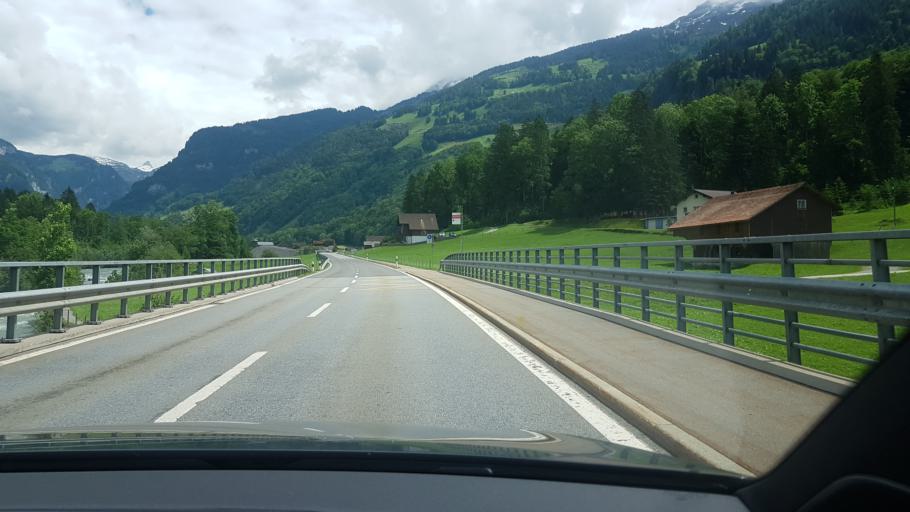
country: CH
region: Schwyz
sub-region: Bezirk Schwyz
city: Muotathal
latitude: 46.9790
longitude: 8.7311
